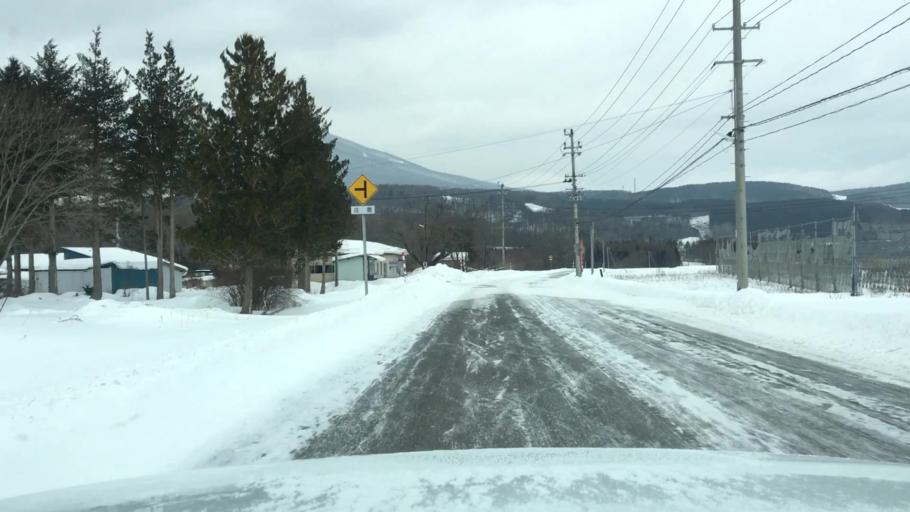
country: JP
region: Iwate
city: Shizukuishi
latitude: 39.9327
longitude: 141.0023
